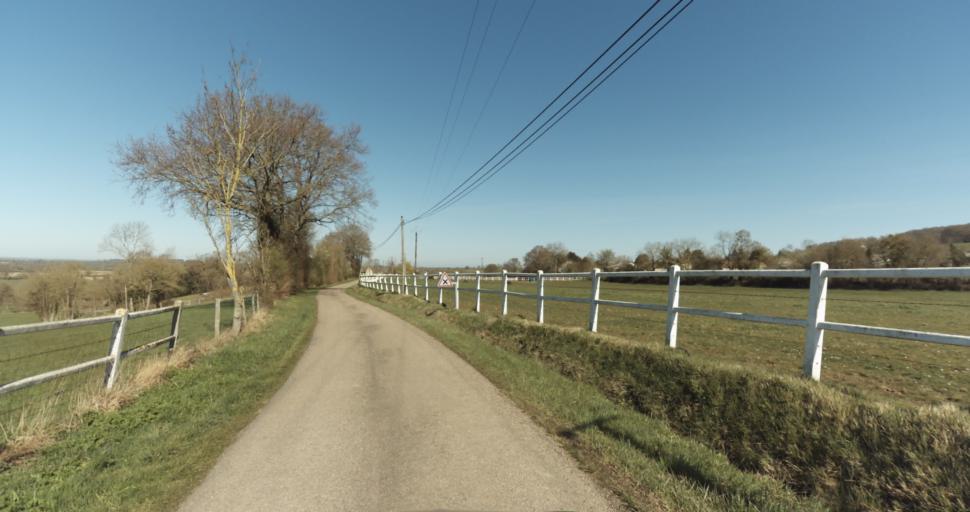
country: FR
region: Lower Normandy
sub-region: Departement de l'Orne
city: Trun
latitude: 48.9298
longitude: 0.0464
